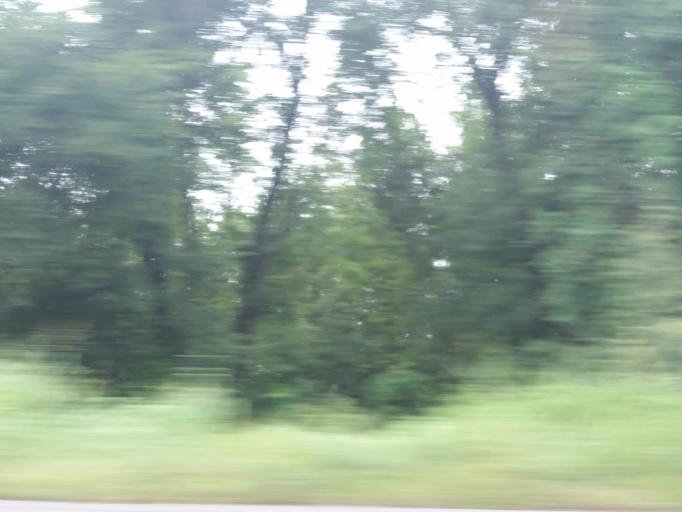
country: US
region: Illinois
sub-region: Alexander County
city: Cairo
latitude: 36.9993
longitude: -89.1320
